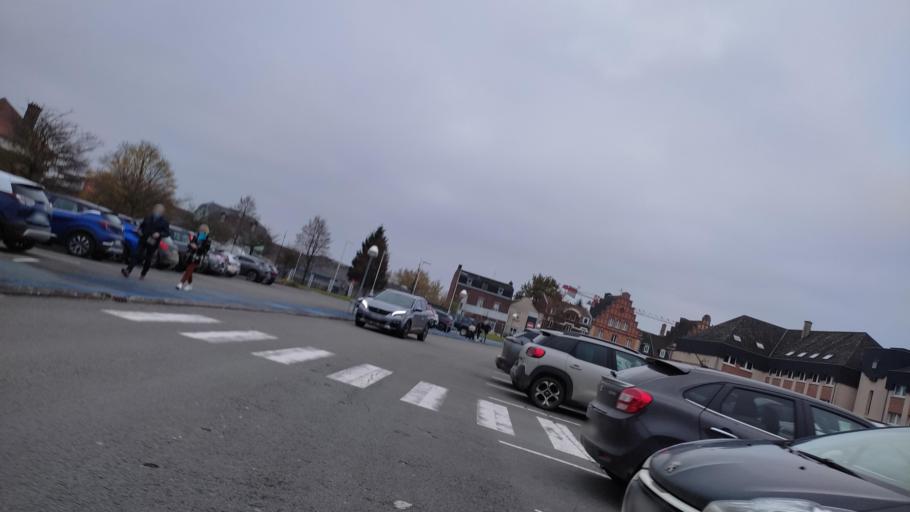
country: FR
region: Nord-Pas-de-Calais
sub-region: Departement du Pas-de-Calais
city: Arras
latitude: 50.2926
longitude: 2.7906
